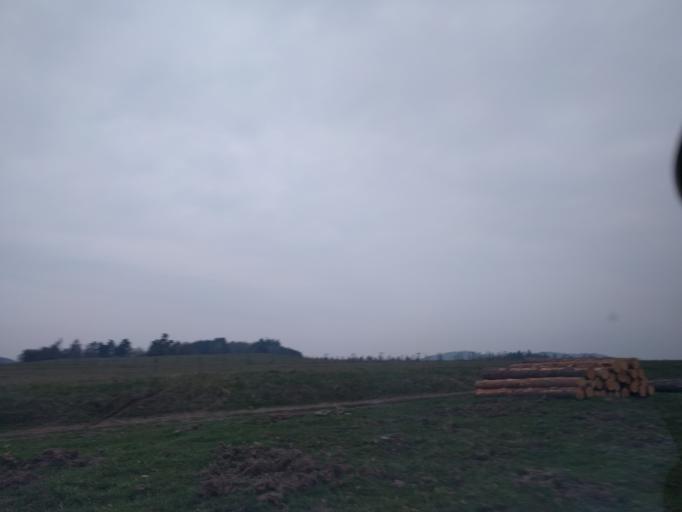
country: CZ
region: Karlovarsky
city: Zlutice
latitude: 50.0986
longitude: 13.0974
